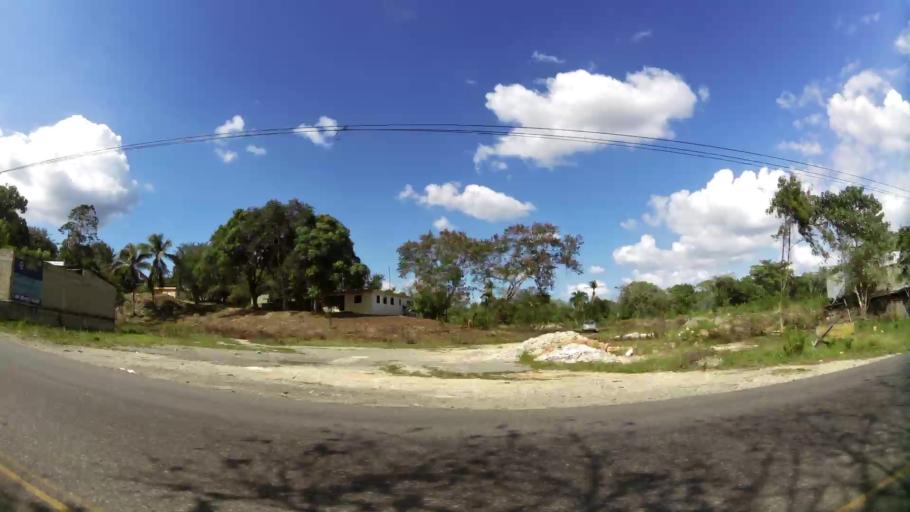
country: DO
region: San Cristobal
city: Bajos de Haina
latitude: 18.4276
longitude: -70.0596
